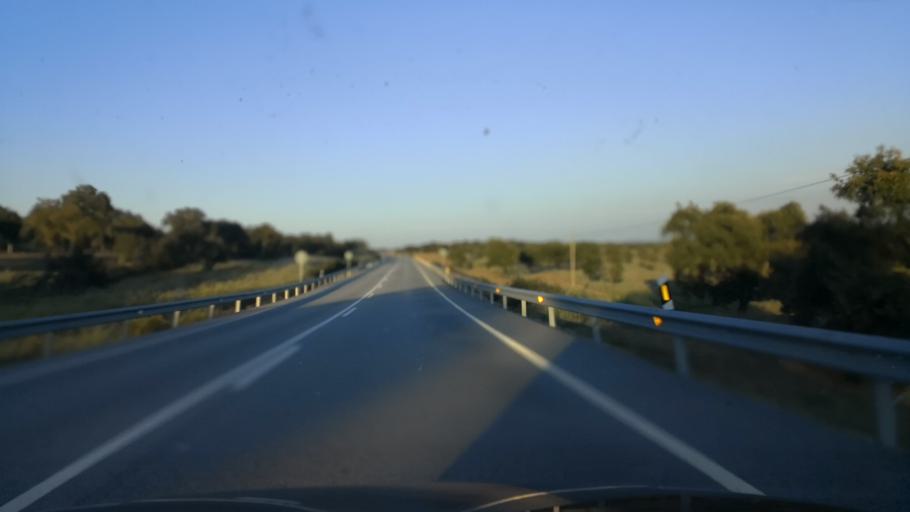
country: ES
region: Extremadura
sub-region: Provincia de Caceres
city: Carbajo
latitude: 39.5071
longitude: -7.1310
